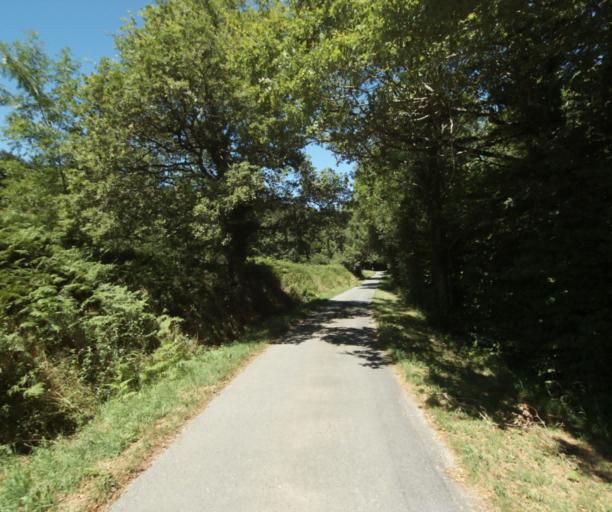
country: FR
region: Midi-Pyrenees
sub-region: Departement du Tarn
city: Dourgne
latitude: 43.4298
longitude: 2.1574
